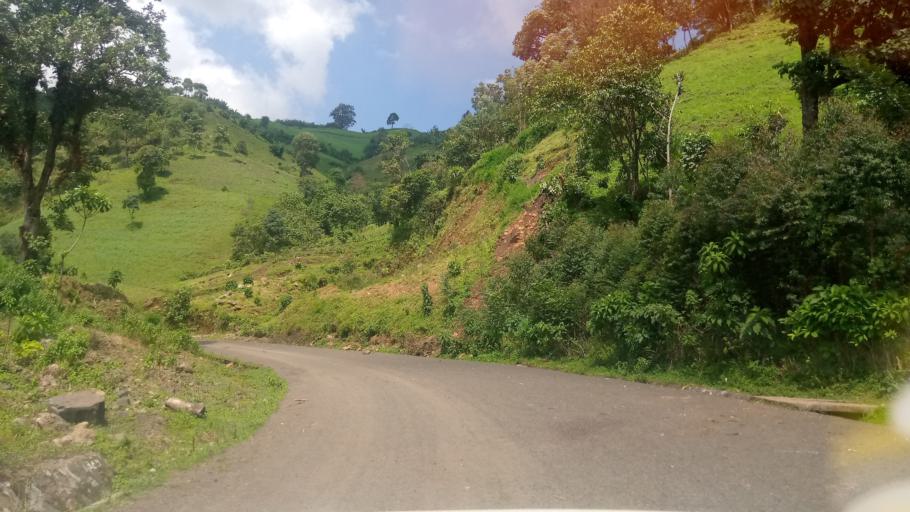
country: ET
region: Southern Nations, Nationalities, and People's Region
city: Bonga
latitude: 7.1469
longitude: 36.5726
